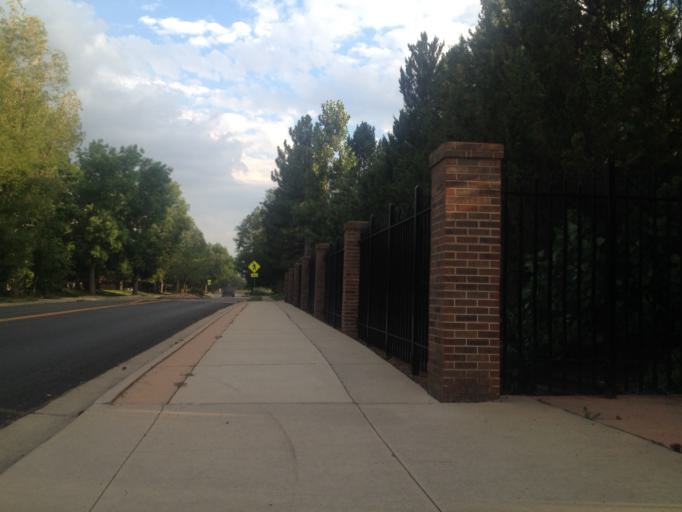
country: US
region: Colorado
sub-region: Boulder County
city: Boulder
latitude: 39.9891
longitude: -105.2236
